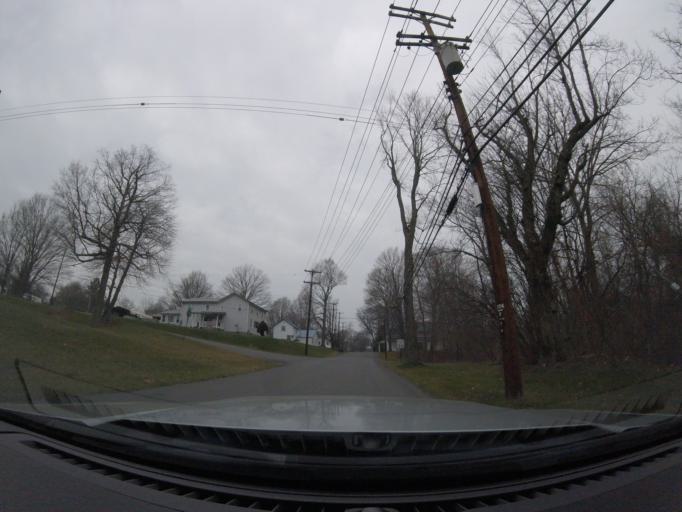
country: US
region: New York
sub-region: Yates County
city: Penn Yan
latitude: 42.6810
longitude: -76.9539
